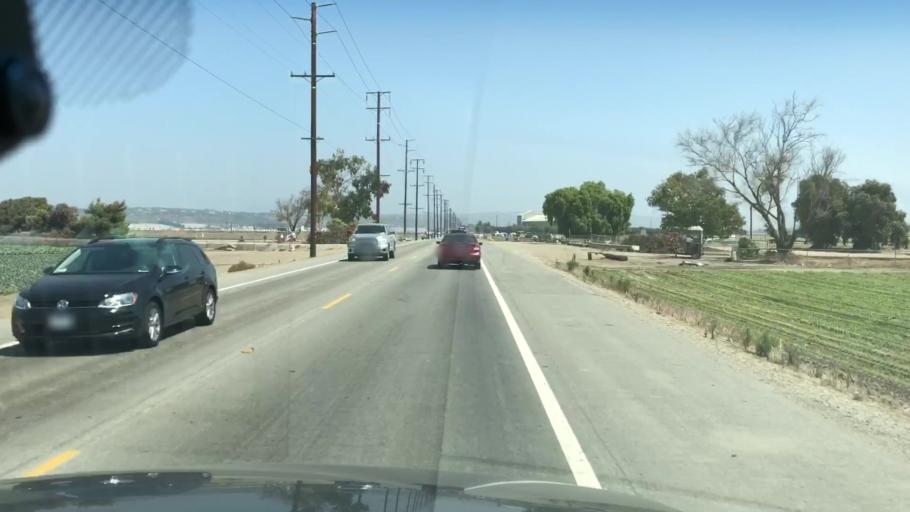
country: US
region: California
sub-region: Ventura County
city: Oxnard
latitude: 34.1920
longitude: -119.1088
